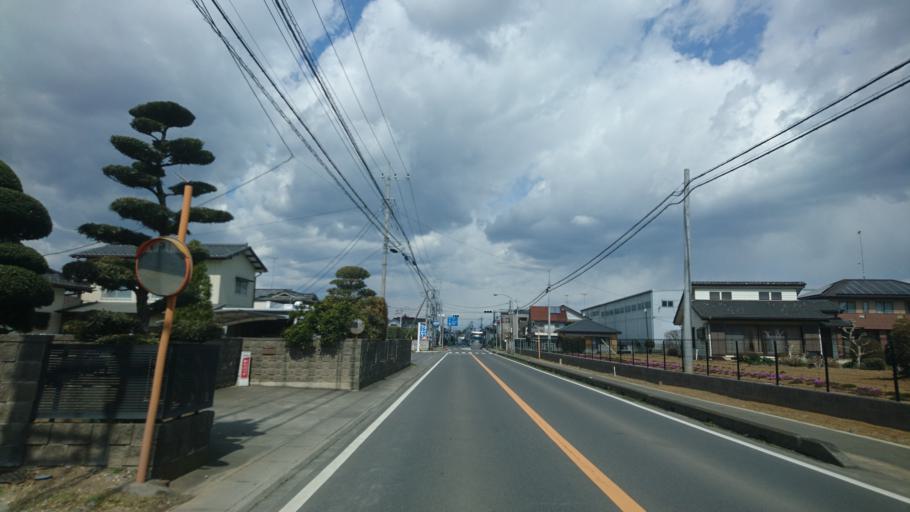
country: JP
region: Ibaraki
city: Shimodate
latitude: 36.2123
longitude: 139.9377
